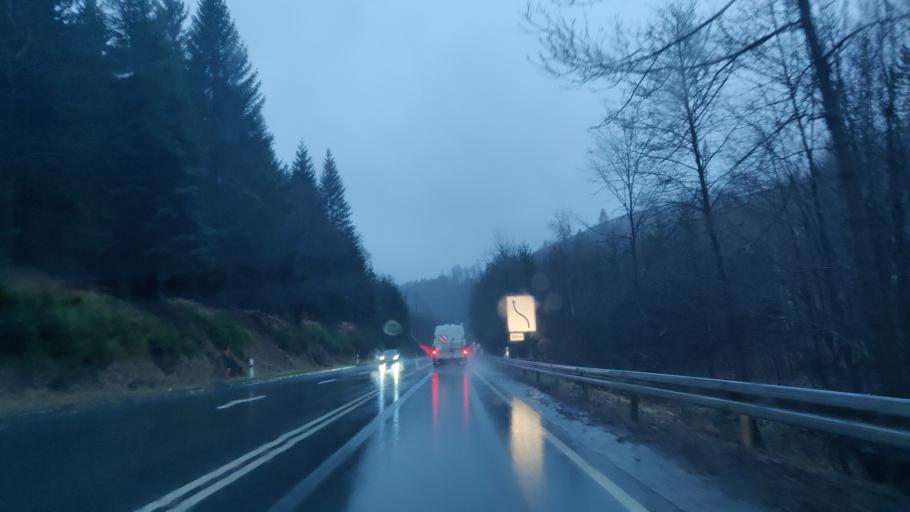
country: DE
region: Lower Saxony
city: Braunlage
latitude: 51.7031
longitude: 10.5805
